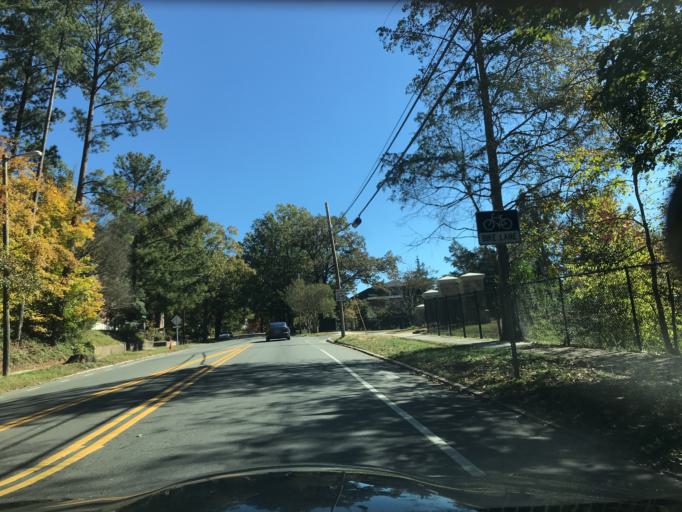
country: US
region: North Carolina
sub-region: Durham County
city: Durham
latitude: 35.9973
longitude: -78.9246
